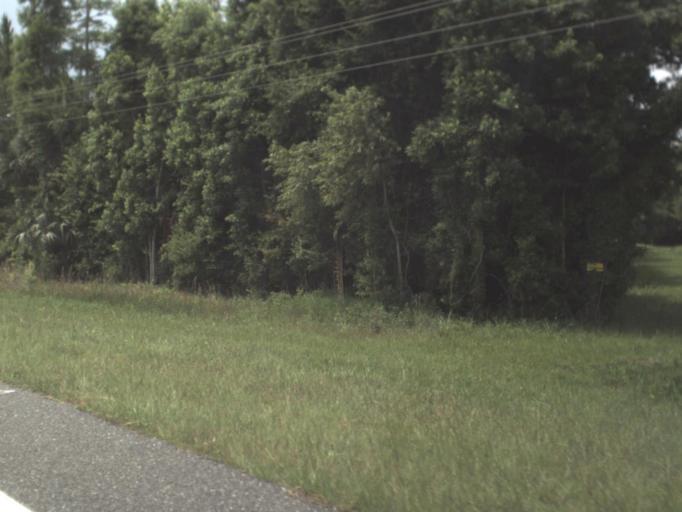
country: US
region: Florida
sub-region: Levy County
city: Chiefland
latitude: 29.3361
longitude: -82.7740
